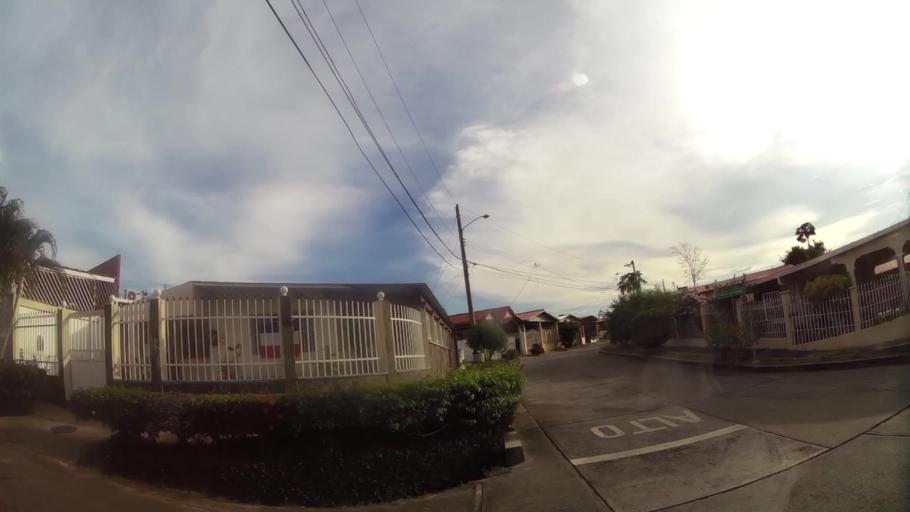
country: PA
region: Panama
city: La Chorrera
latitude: 8.8968
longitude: -79.7685
